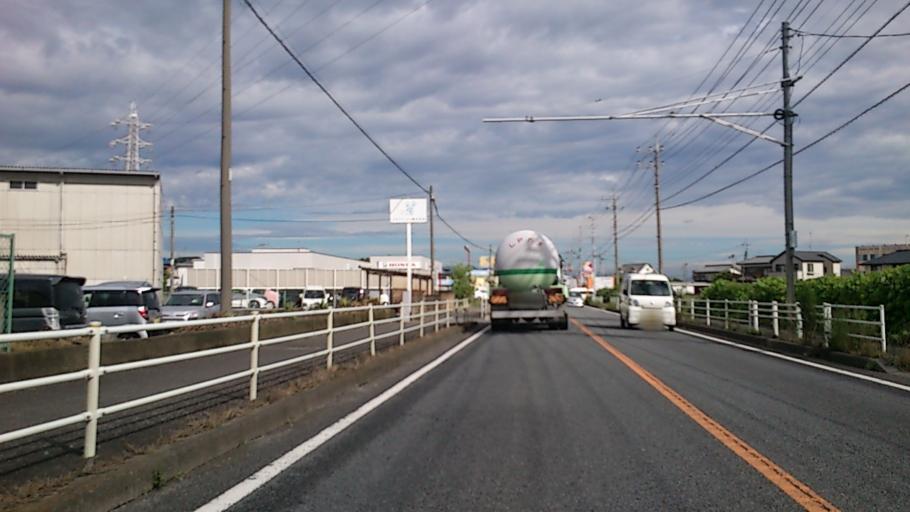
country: JP
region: Saitama
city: Honjo
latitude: 36.2377
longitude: 139.2059
